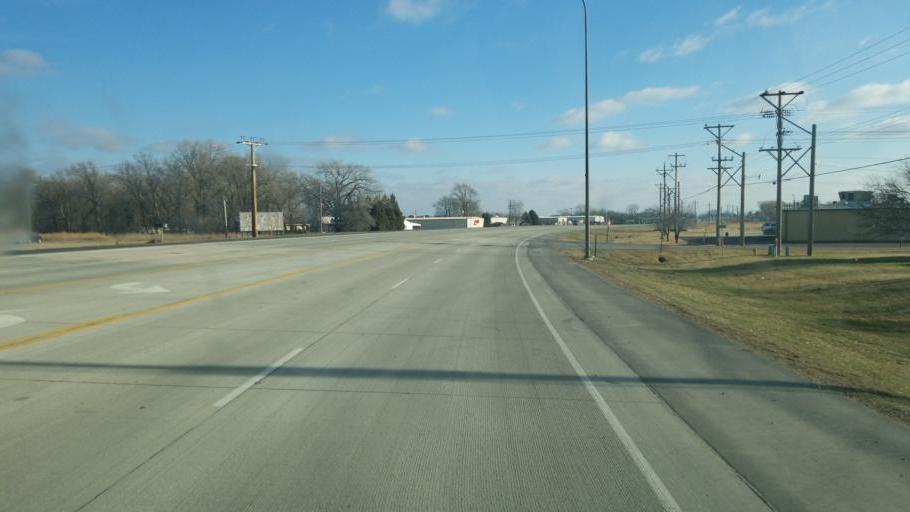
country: US
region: South Dakota
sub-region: Yankton County
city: Yankton
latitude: 42.8792
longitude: -97.3641
